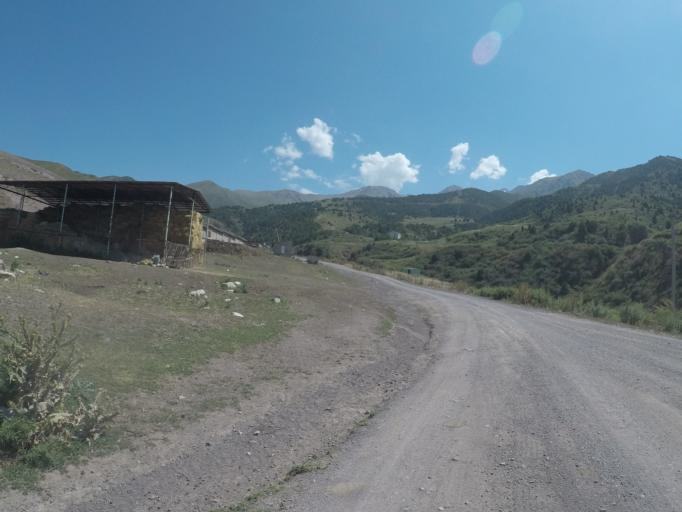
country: KG
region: Chuy
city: Bishkek
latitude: 42.6482
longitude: 74.5125
